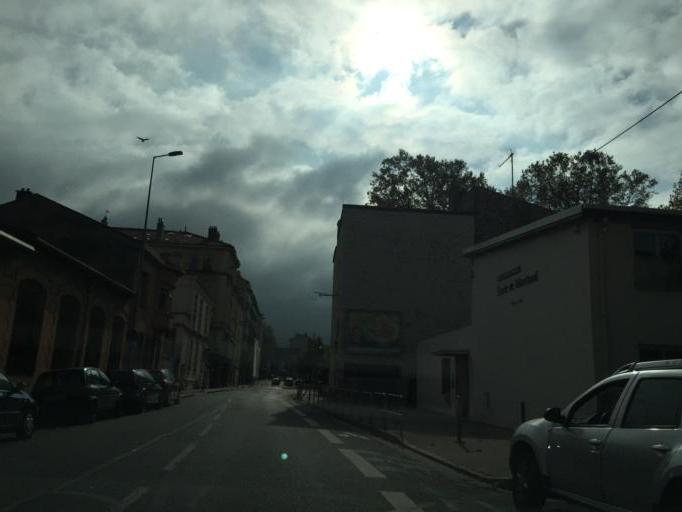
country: FR
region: Rhone-Alpes
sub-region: Departement de la Loire
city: Saint-Etienne
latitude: 45.4487
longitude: 4.3821
